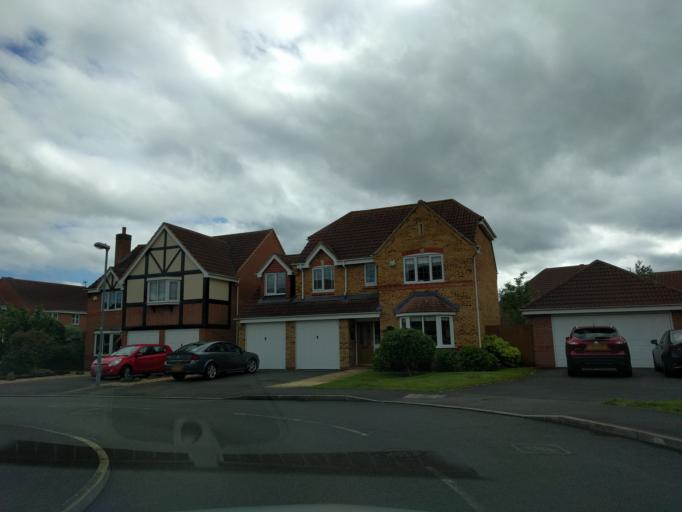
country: GB
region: England
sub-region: Nottinghamshire
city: Newark on Trent
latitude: 53.0787
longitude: -0.7804
